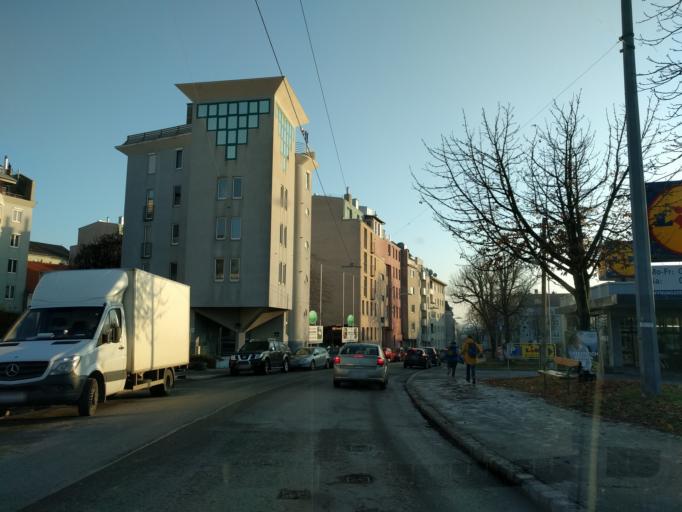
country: AT
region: Lower Austria
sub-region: Politischer Bezirk Modling
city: Perchtoldsdorf
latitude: 48.1988
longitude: 16.2806
